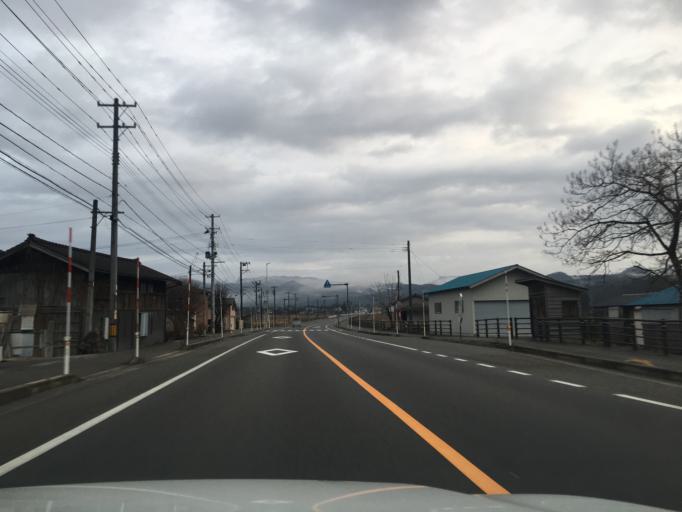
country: JP
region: Niigata
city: Murakami
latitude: 38.3184
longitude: 139.5514
